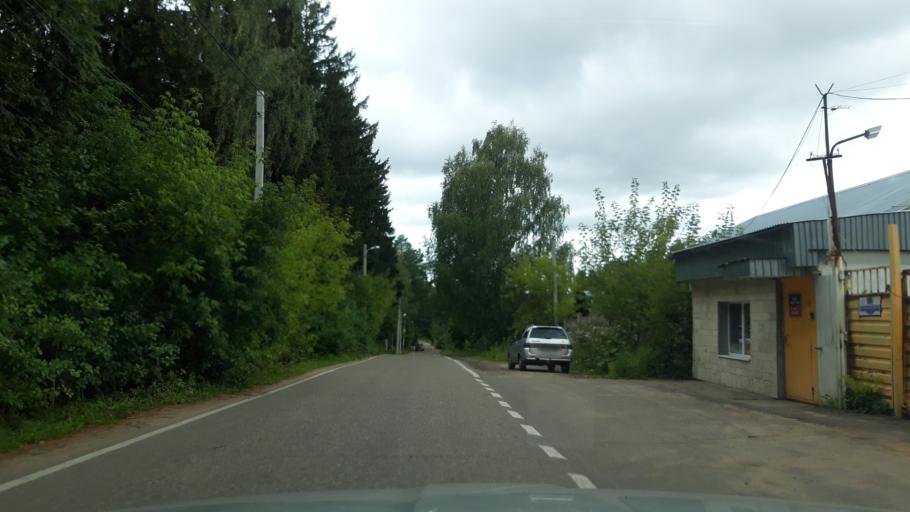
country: RU
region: Moskovskaya
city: Povarovo
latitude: 56.0627
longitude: 37.0660
